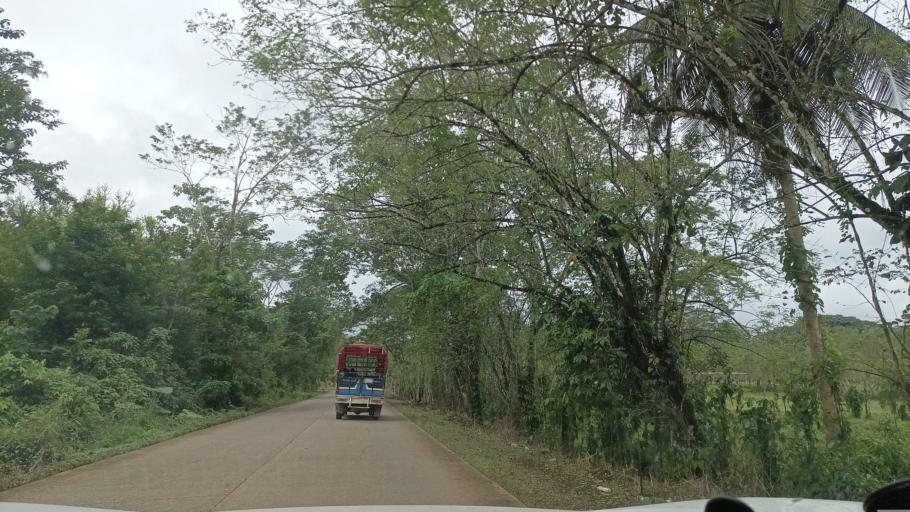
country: MX
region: Veracruz
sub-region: Uxpanapa
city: Poblado 10
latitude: 17.2788
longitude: -94.4814
